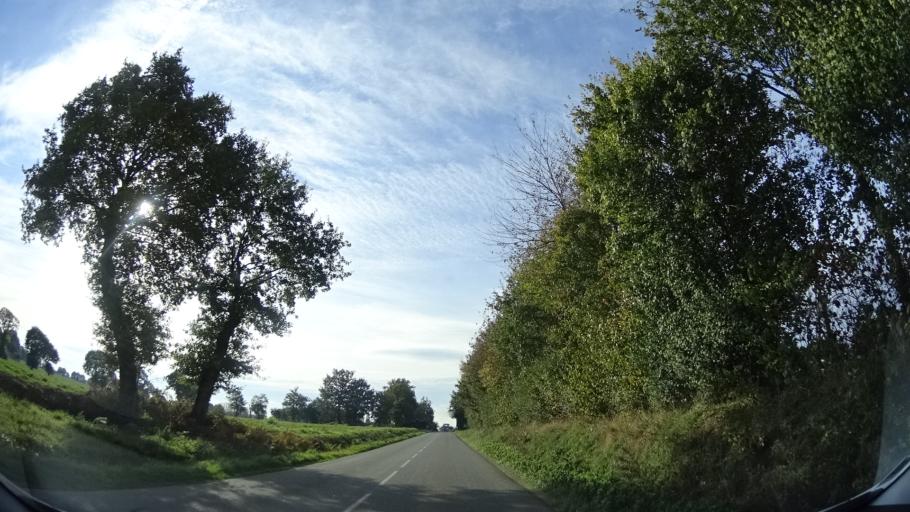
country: FR
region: Brittany
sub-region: Departement d'Ille-et-Vilaine
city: Pleumeleuc
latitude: 48.2102
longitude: -1.9352
